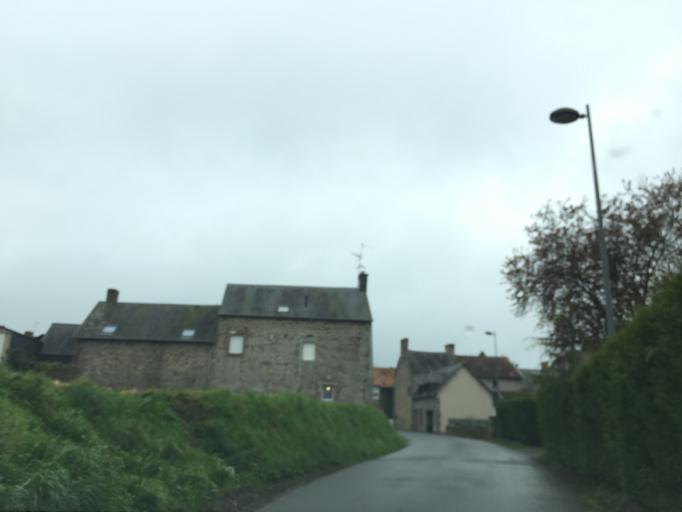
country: FR
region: Lower Normandy
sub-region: Departement de la Manche
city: Saint-James
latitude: 48.5636
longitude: -1.3993
